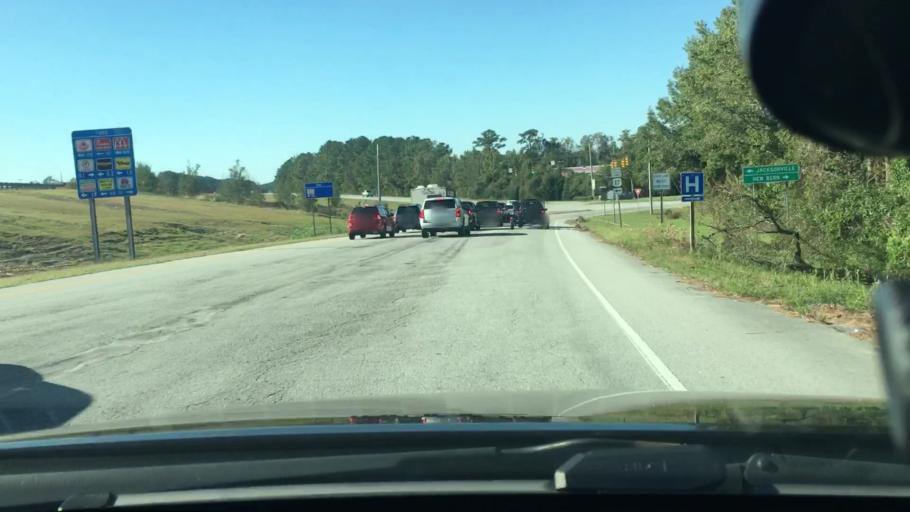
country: US
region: North Carolina
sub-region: Craven County
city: Trent Woods
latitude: 35.1034
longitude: -77.0825
